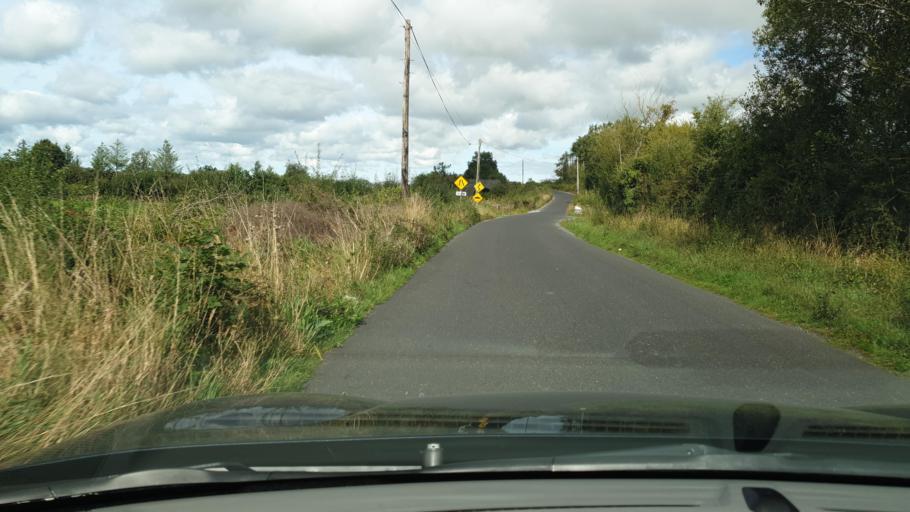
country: IE
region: Leinster
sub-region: Laois
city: Portlaoise
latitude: 53.0704
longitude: -7.2697
